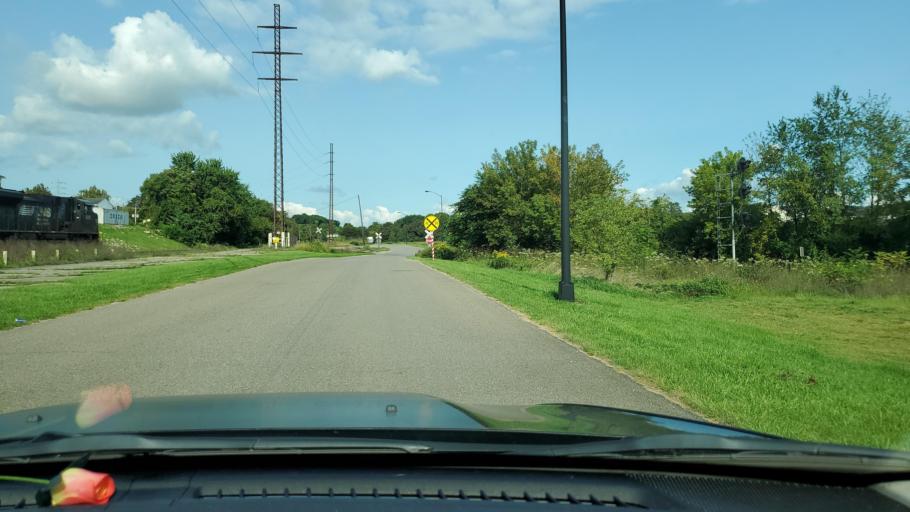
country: US
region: Ohio
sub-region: Mahoning County
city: Struthers
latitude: 41.0599
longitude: -80.5938
